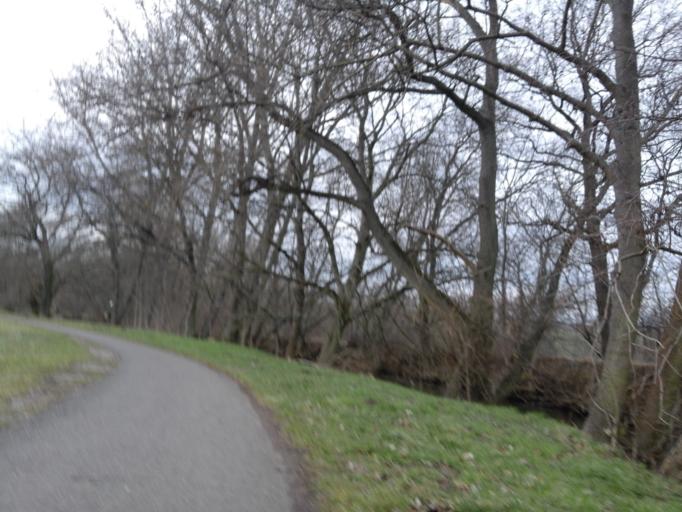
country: DE
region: Thuringia
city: Kromsdorf
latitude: 50.9976
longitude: 11.3598
